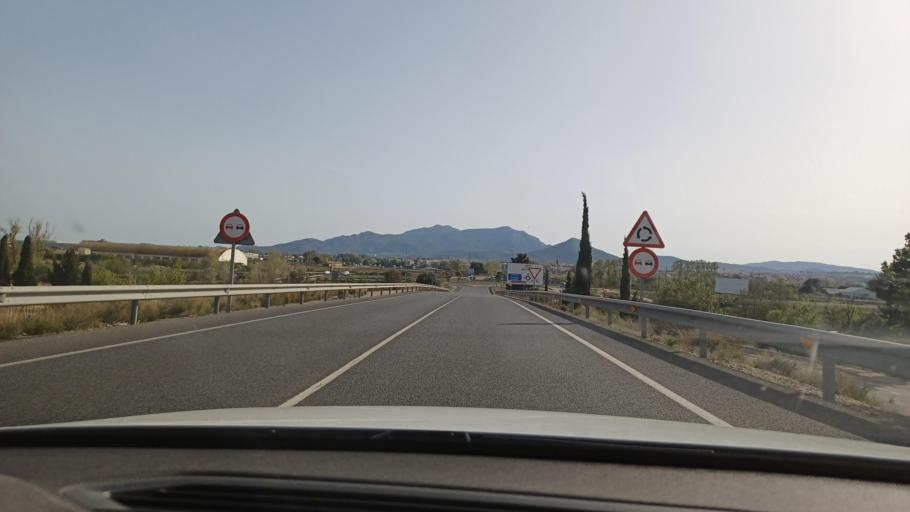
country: ES
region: Catalonia
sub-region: Provincia de Tarragona
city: Amposta
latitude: 40.7247
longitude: 0.5902
